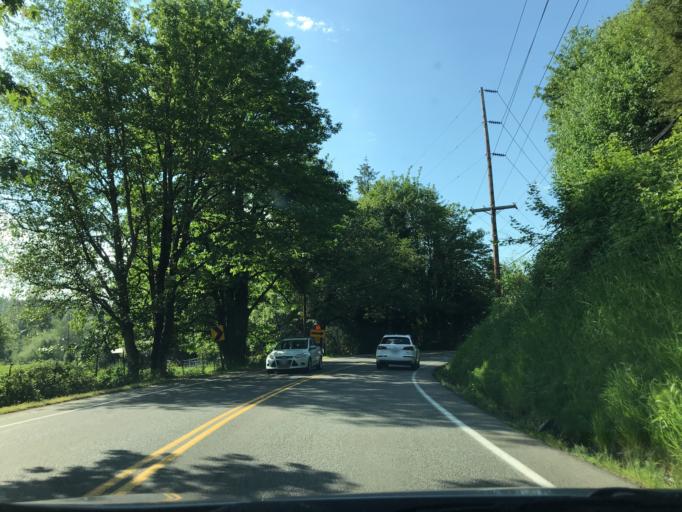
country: US
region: Washington
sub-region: King County
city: Mirrormont
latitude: 47.4433
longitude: -121.9876
